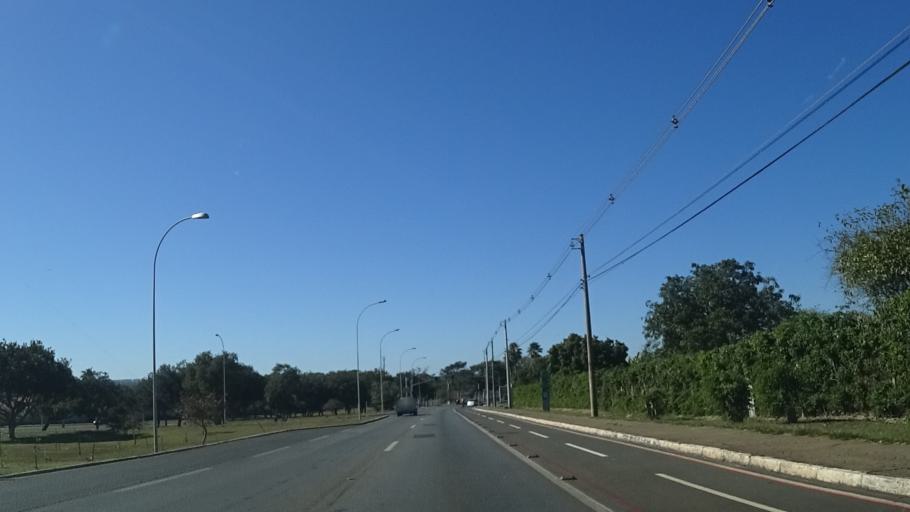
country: BR
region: Federal District
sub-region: Brasilia
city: Brasilia
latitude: -15.7284
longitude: -47.8712
